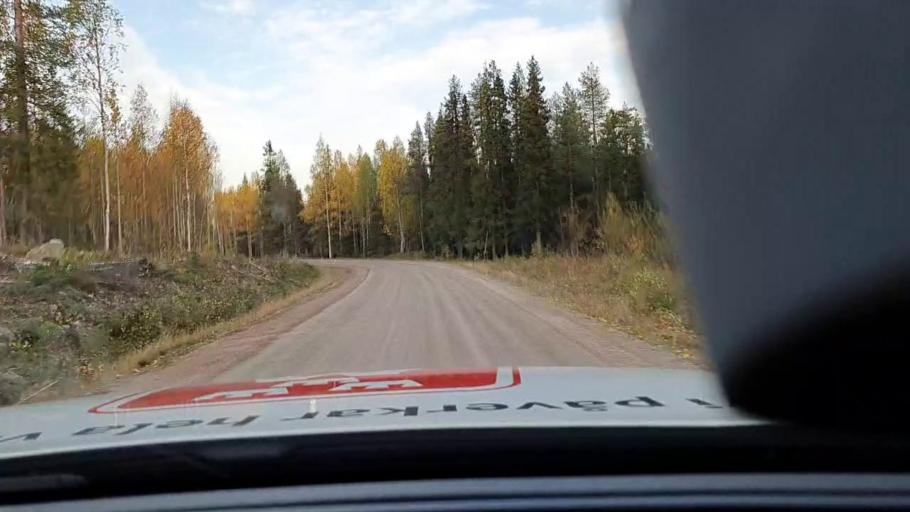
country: SE
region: Norrbotten
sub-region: Overkalix Kommun
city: OEverkalix
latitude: 66.3174
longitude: 22.6704
